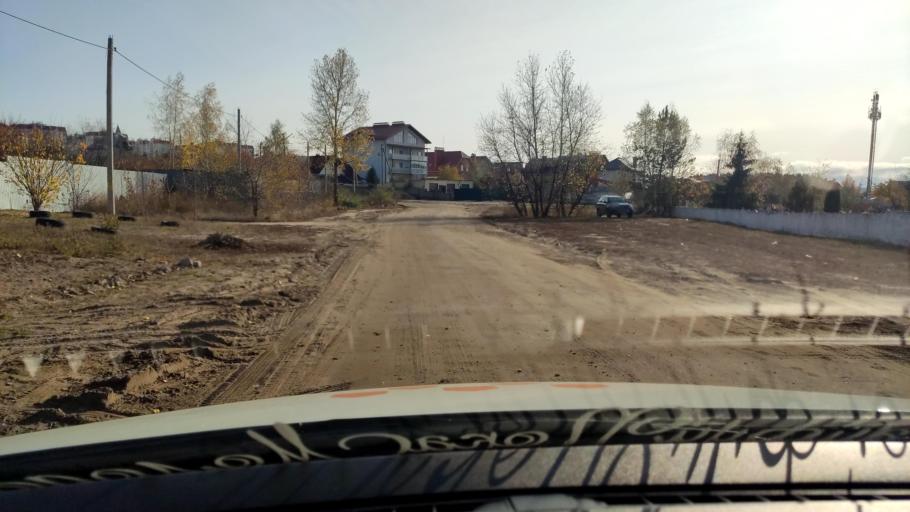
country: RU
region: Voronezj
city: Pridonskoy
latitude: 51.6553
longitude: 39.0948
